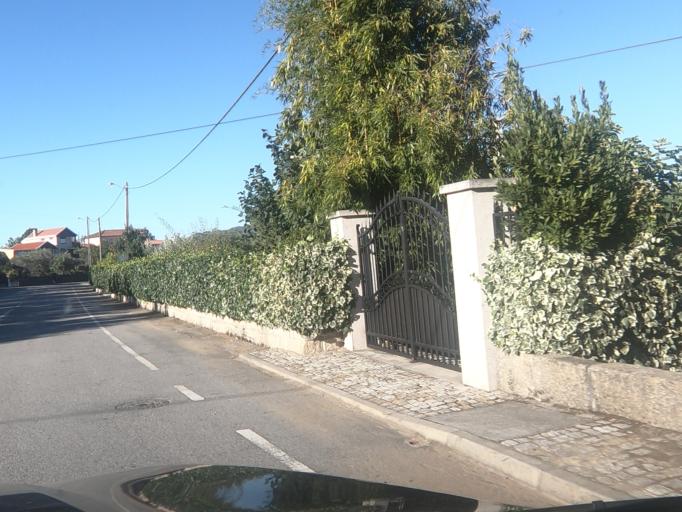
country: PT
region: Vila Real
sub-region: Sabrosa
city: Sabrosa
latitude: 41.3164
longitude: -7.5816
